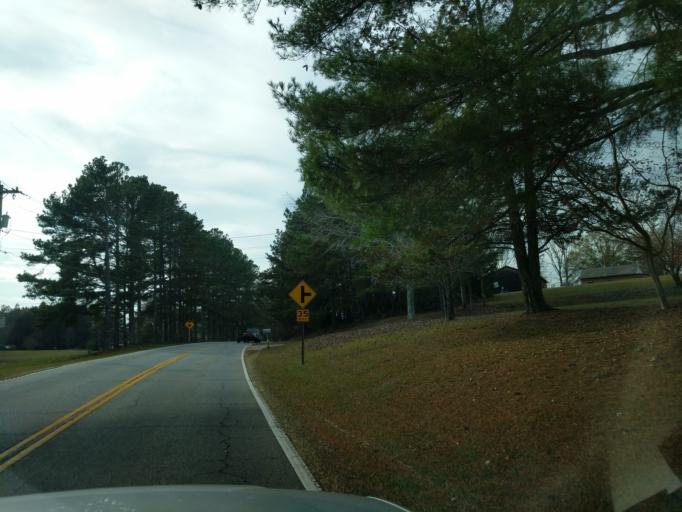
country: US
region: South Carolina
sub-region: Pickens County
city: Central
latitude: 34.8329
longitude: -82.8357
